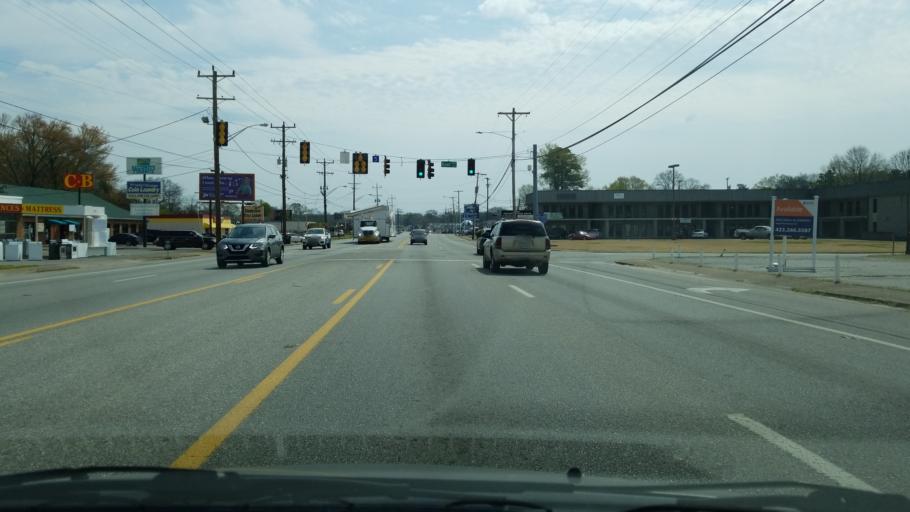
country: US
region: Tennessee
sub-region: Hamilton County
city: East Ridge
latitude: 34.9930
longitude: -85.2287
